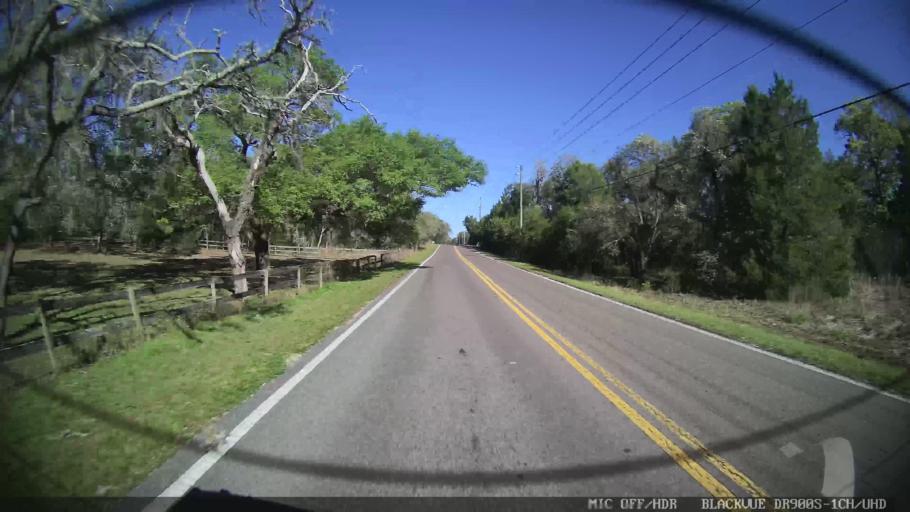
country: US
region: Florida
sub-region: Pasco County
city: Shady Hills
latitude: 28.3920
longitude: -82.5688
